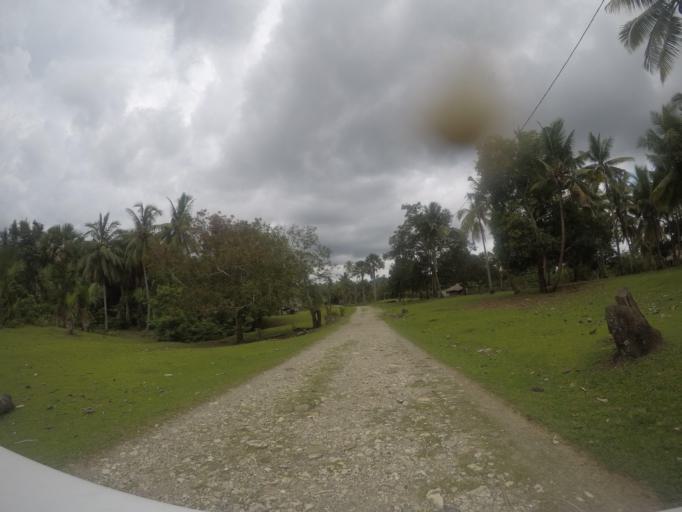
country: TL
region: Viqueque
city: Viqueque
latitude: -8.8537
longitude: 126.3526
